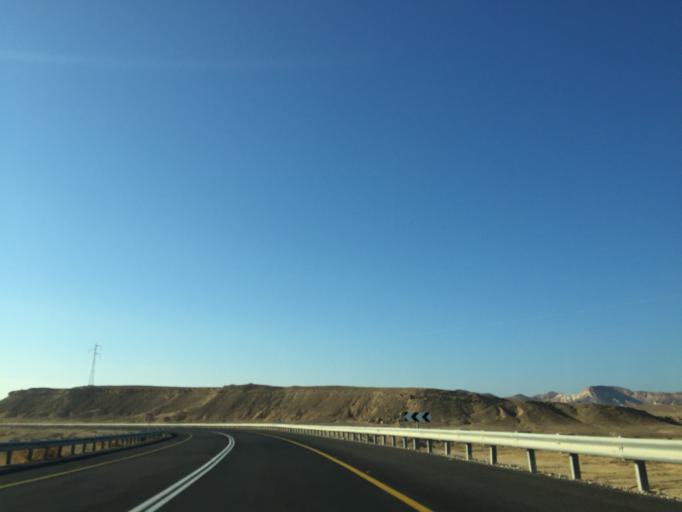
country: IL
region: Southern District
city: Mitzpe Ramon
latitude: 30.3049
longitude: 34.9662
